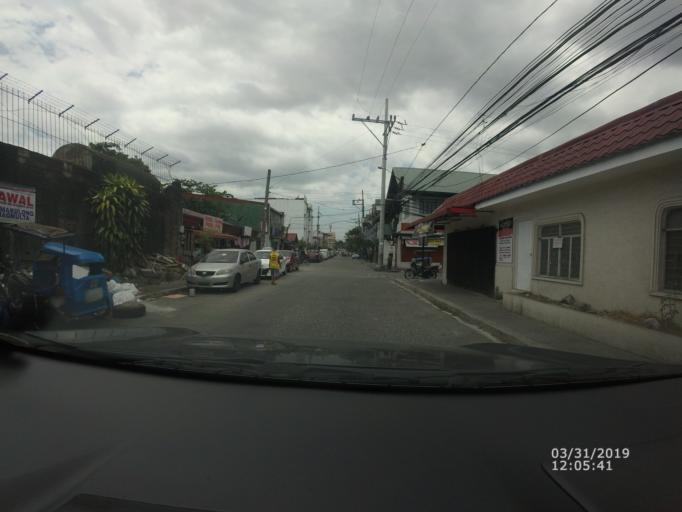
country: PH
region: Metro Manila
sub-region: Mandaluyong
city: Mandaluyong City
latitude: 14.5804
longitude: 121.0334
